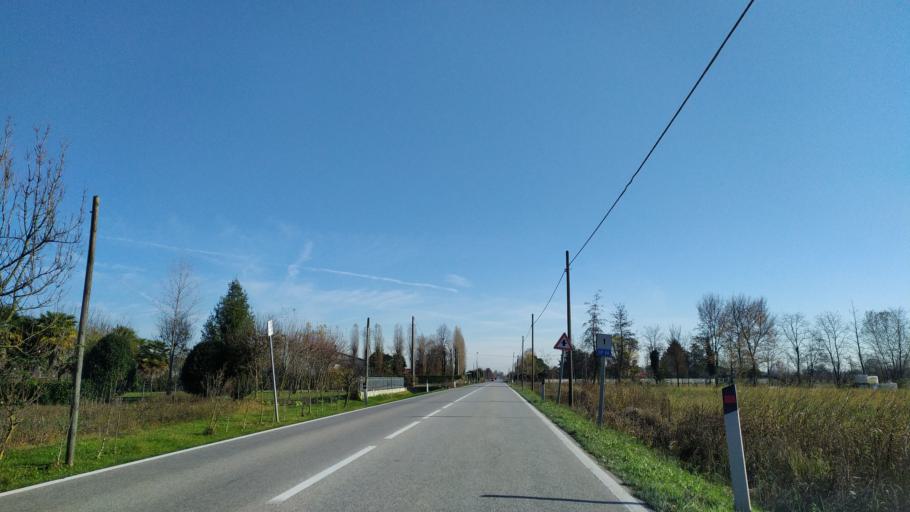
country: IT
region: Veneto
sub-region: Provincia di Padova
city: San Giorgio in Bosco
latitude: 45.5877
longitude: 11.8188
